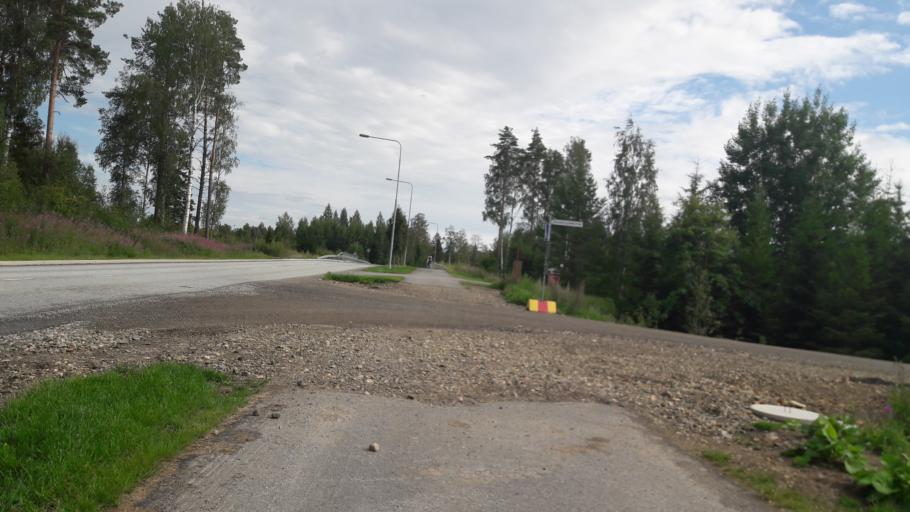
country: FI
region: North Karelia
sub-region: Joensuu
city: Joensuu
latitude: 62.5697
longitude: 29.8235
